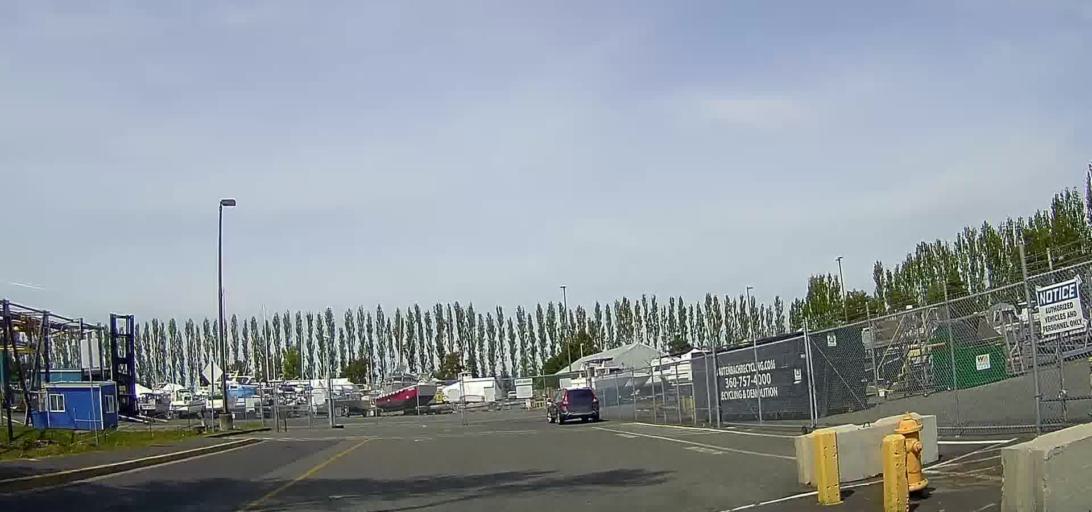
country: US
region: Washington
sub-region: Skagit County
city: Mount Vernon
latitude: 48.4007
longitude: -122.4927
